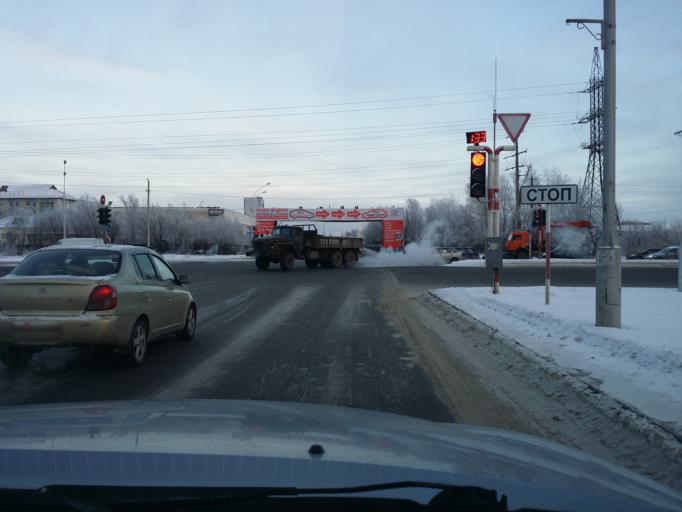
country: RU
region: Khanty-Mansiyskiy Avtonomnyy Okrug
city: Nizhnevartovsk
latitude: 60.9482
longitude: 76.5287
